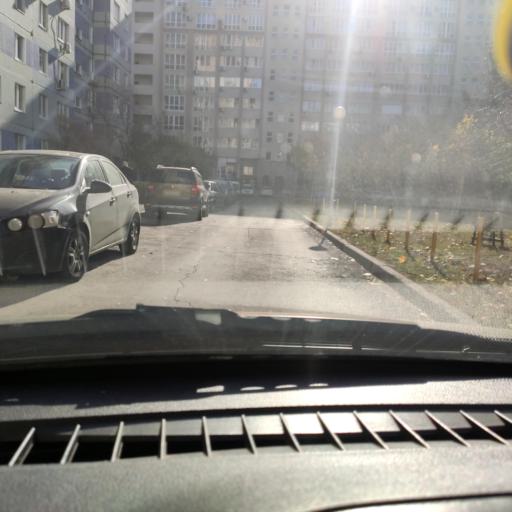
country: RU
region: Samara
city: Tol'yatti
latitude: 53.5408
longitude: 49.3409
